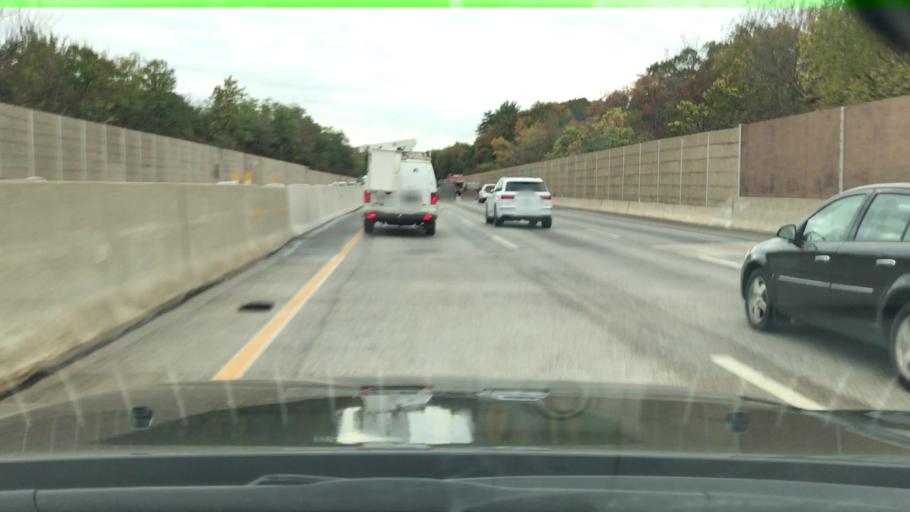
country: US
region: Pennsylvania
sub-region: Montgomery County
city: Fort Washington
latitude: 40.1262
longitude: -75.2237
